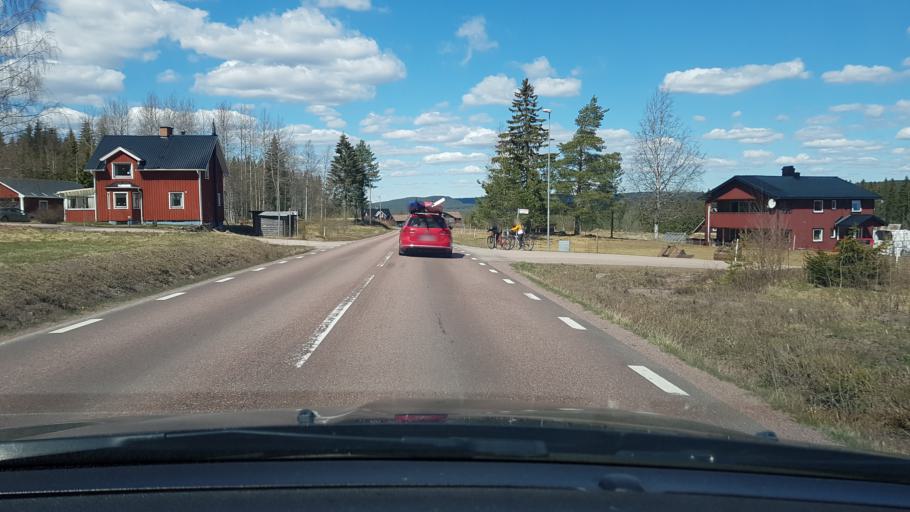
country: SE
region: Dalarna
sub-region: Alvdalens Kommun
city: AElvdalen
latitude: 61.1355
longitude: 13.9482
